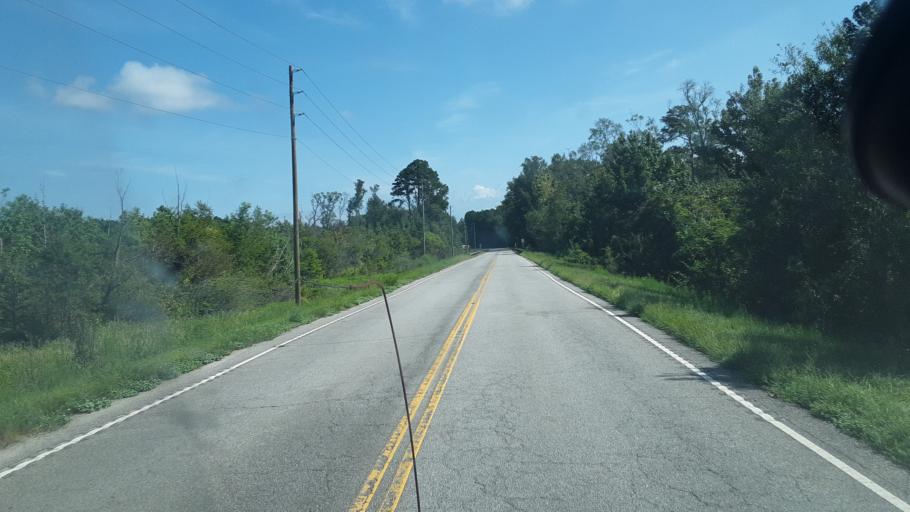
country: US
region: South Carolina
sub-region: Hampton County
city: Varnville
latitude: 32.7973
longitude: -81.0552
